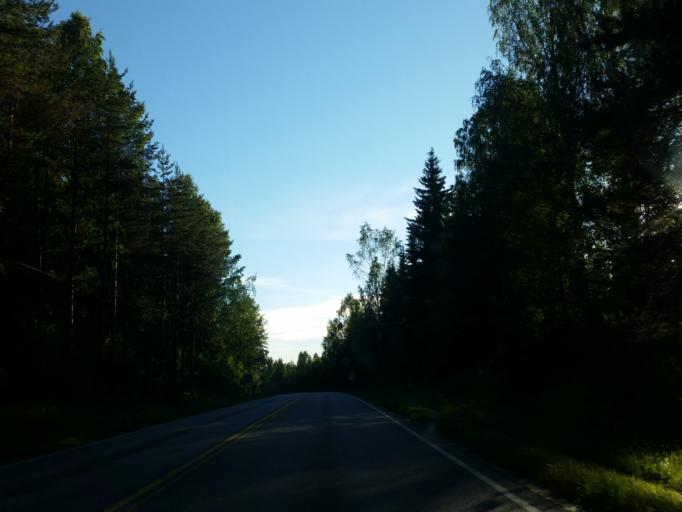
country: FI
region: Northern Savo
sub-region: Kuopio
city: Karttula
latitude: 62.8676
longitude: 27.1625
